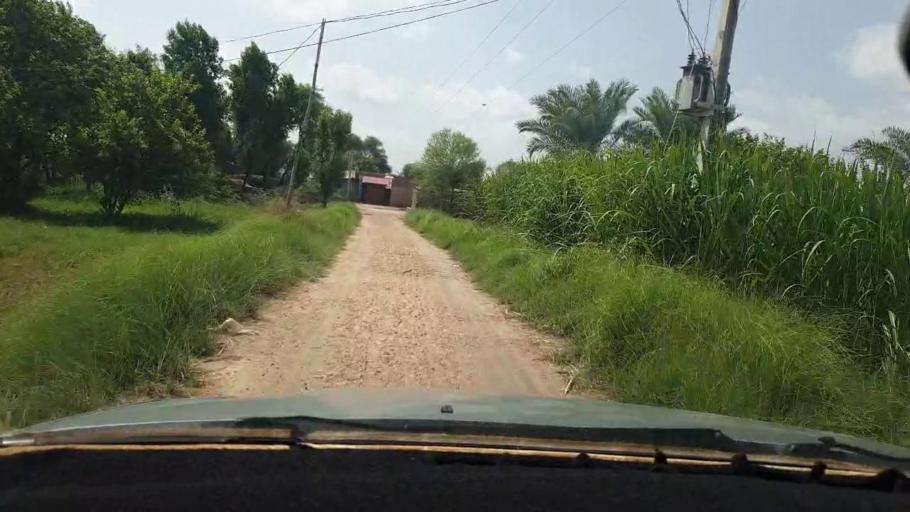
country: PK
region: Sindh
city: Tando Bago
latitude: 24.7538
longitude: 69.1616
